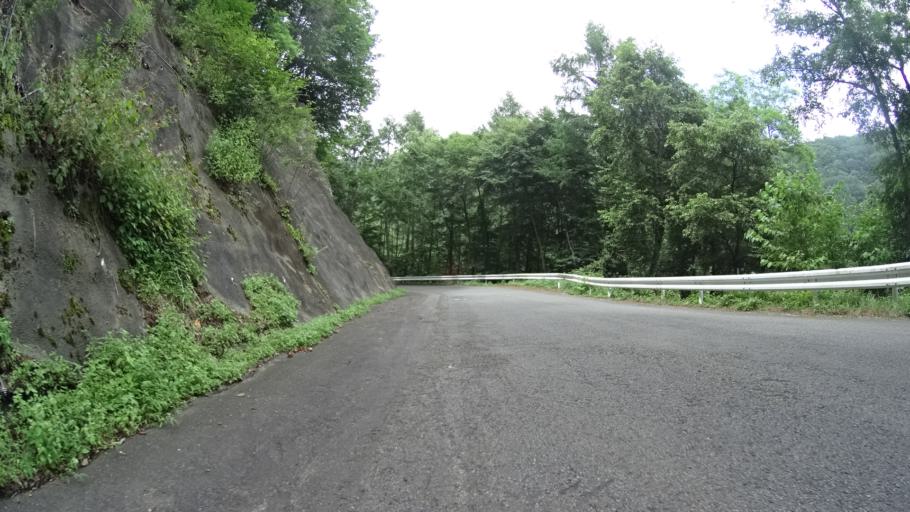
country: JP
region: Nagano
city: Saku
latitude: 36.0708
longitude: 138.6497
